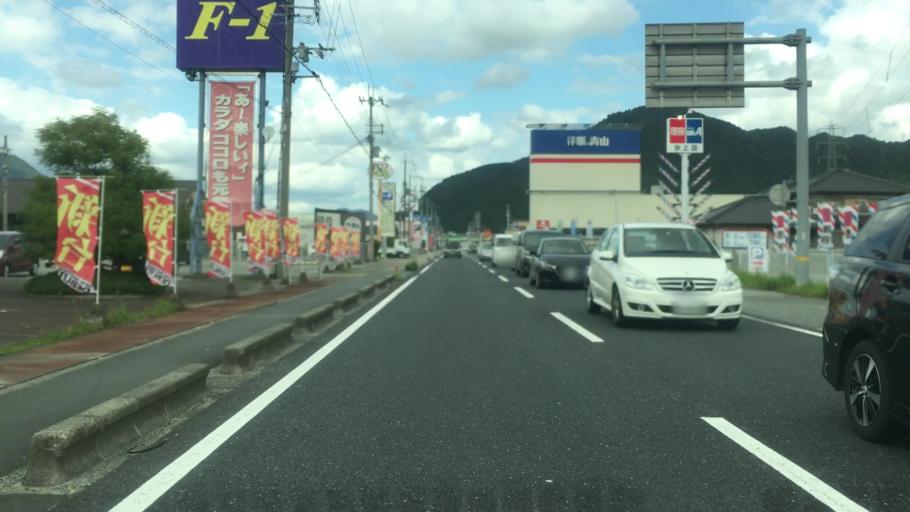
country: JP
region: Kyoto
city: Fukuchiyama
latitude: 35.1549
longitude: 135.0478
